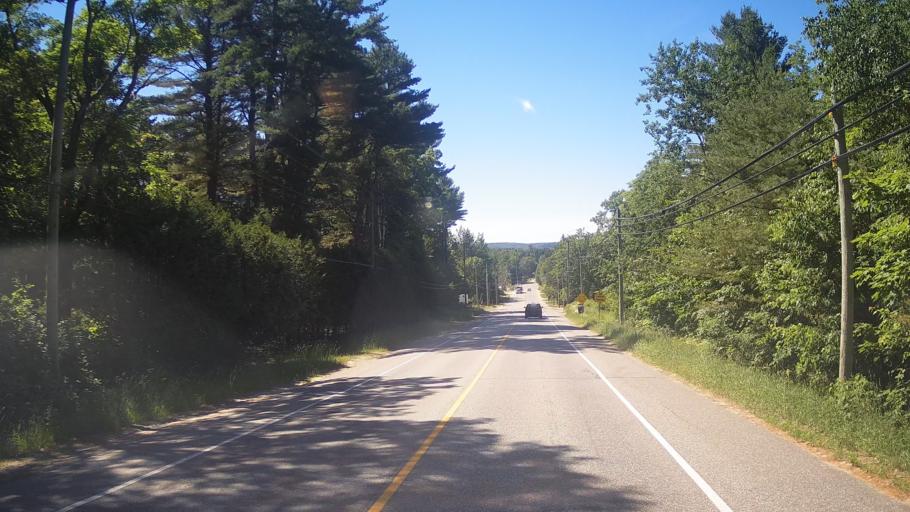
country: CA
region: Ontario
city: Huntsville
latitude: 45.3556
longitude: -79.2028
